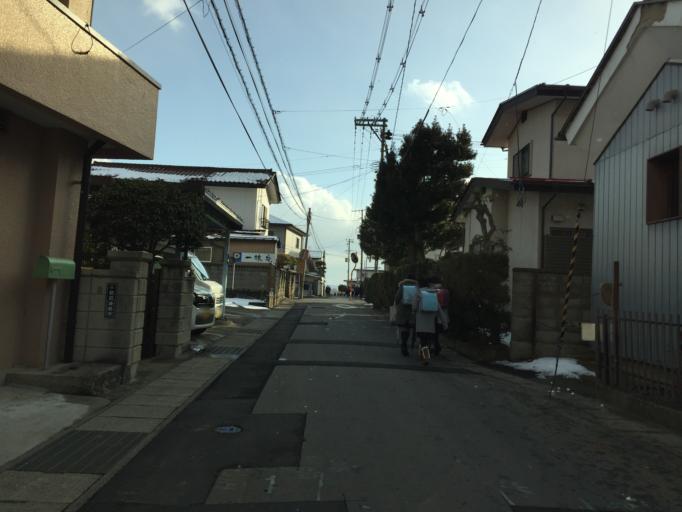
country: JP
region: Fukushima
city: Fukushima-shi
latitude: 37.8315
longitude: 140.4502
